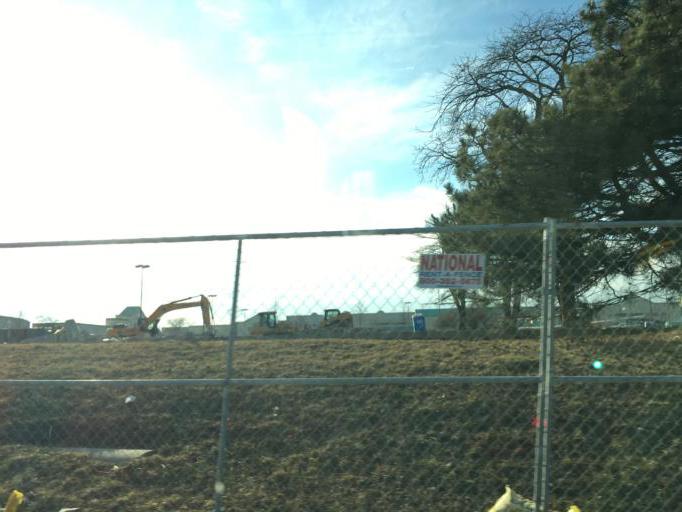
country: US
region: Illinois
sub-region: Cook County
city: Hoffman Estates
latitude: 42.0479
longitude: -88.0799
